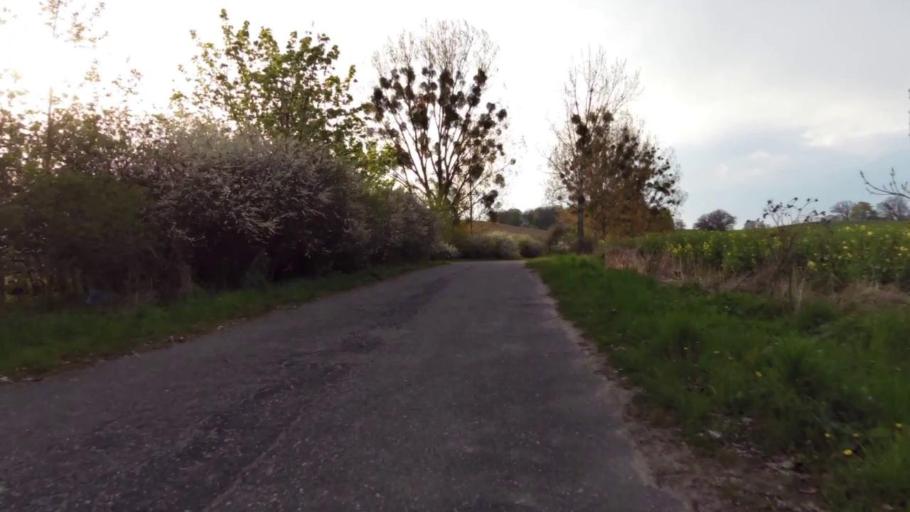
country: PL
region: West Pomeranian Voivodeship
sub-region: Powiat mysliborski
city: Mysliborz
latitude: 52.8953
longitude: 14.7761
